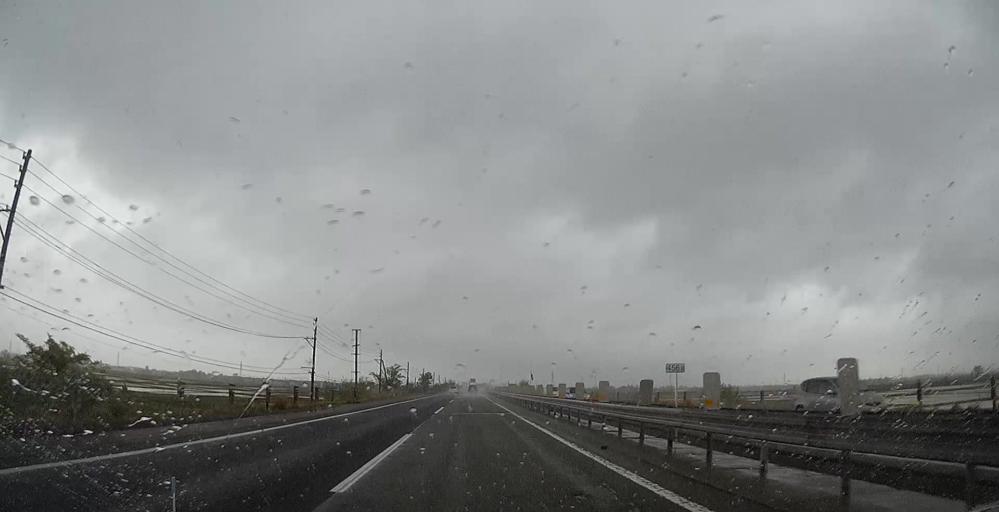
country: JP
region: Niigata
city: Maki
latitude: 37.7361
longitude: 138.9376
